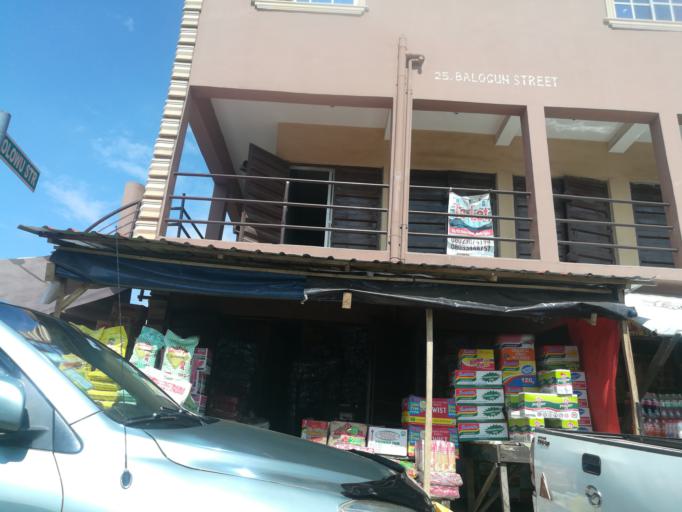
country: NG
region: Lagos
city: Agege
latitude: 6.6241
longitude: 3.3248
